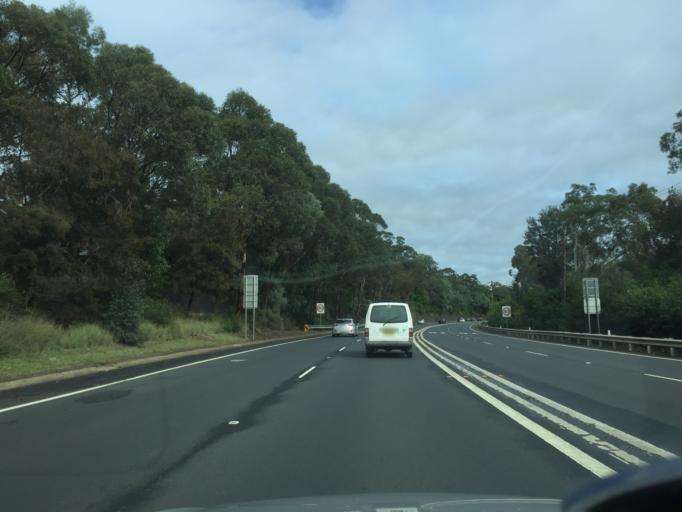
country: AU
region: New South Wales
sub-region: Blue Mountains Municipality
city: Glenbrook
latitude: -33.7638
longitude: 150.6302
